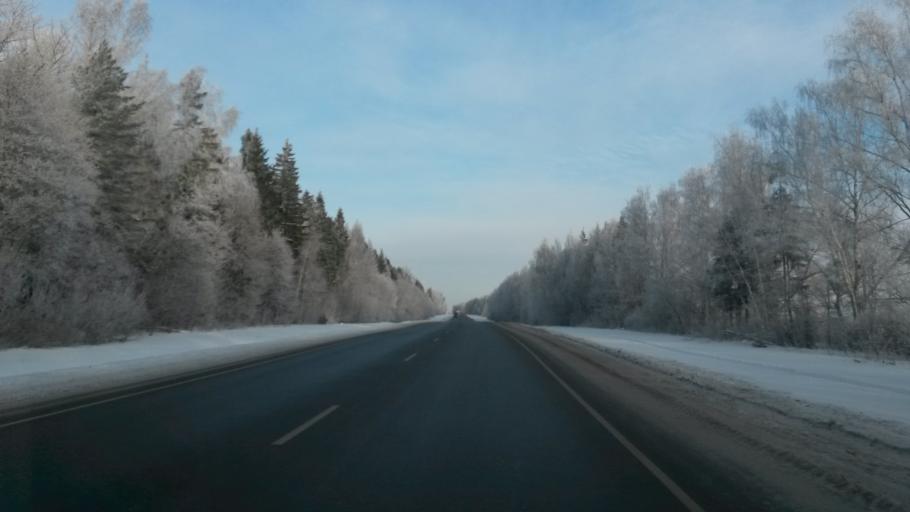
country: RU
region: Vladimir
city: Bogolyubovo
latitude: 56.2285
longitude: 40.4450
